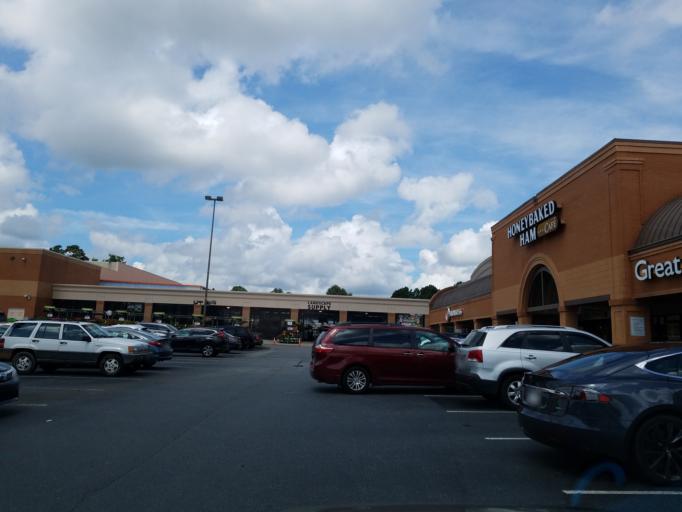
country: US
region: Georgia
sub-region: Fulton County
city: Sandy Springs
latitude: 33.9814
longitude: -84.4340
